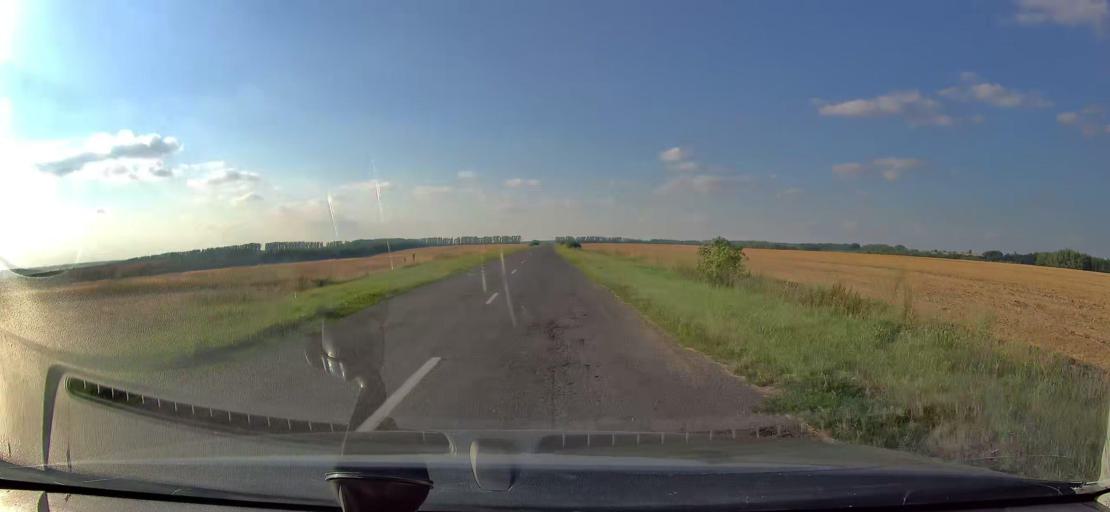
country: RU
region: Kursk
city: Zolotukhino
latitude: 52.0349
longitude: 36.2168
